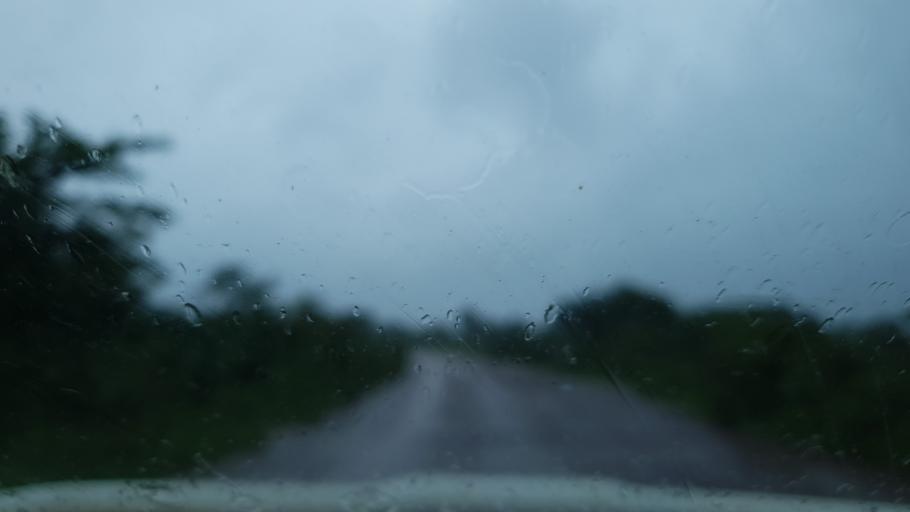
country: ML
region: Sikasso
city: Kolondieba
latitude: 11.6068
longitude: -6.6752
